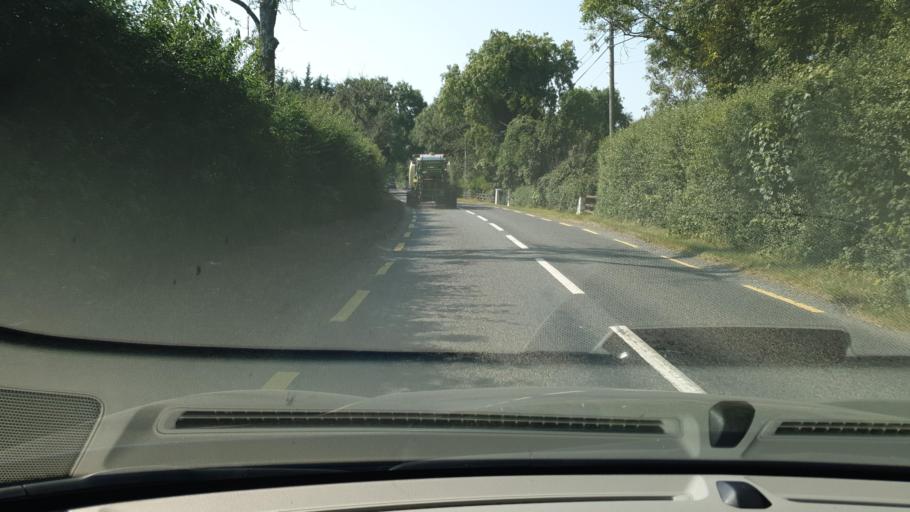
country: IE
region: Leinster
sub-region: An Mhi
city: Trim
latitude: 53.5808
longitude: -6.8443
